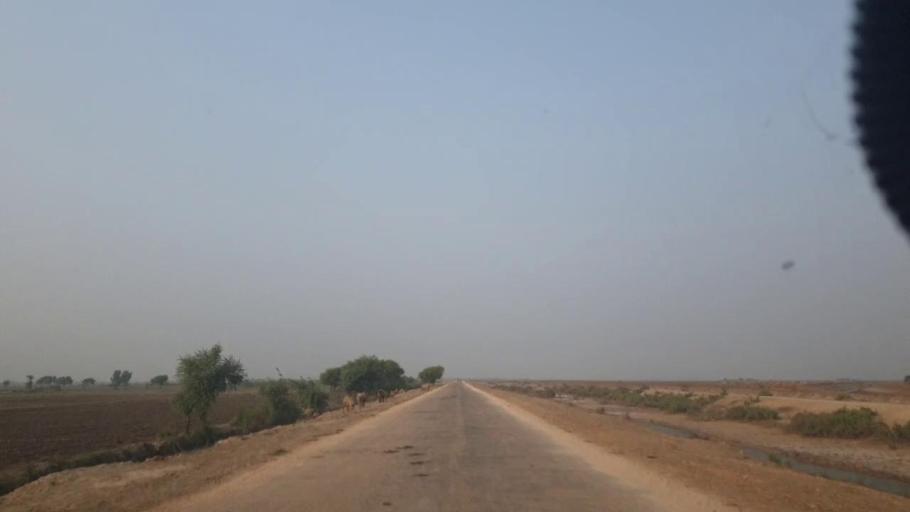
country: PK
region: Sindh
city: Bulri
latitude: 24.8448
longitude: 68.4041
